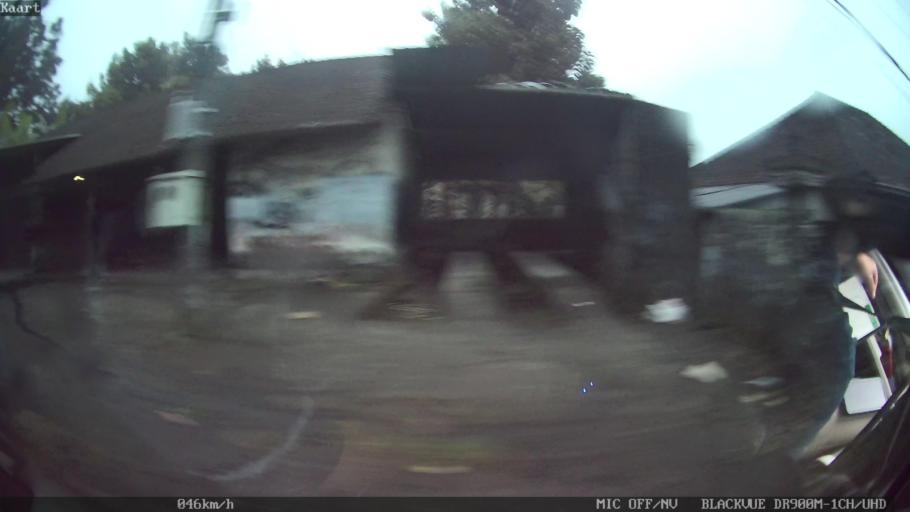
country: ID
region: Bali
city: Banjar Ponggang
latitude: -8.3774
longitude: 115.2673
